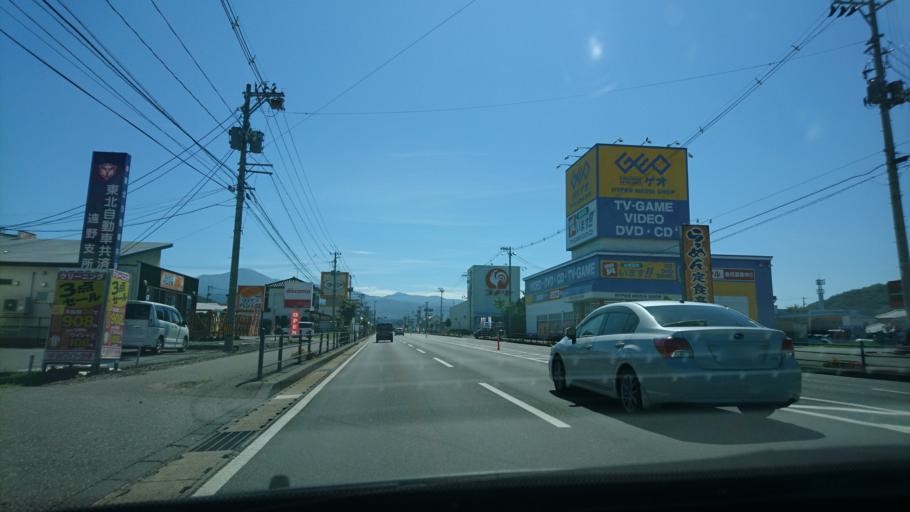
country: JP
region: Iwate
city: Tono
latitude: 39.3376
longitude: 141.5434
